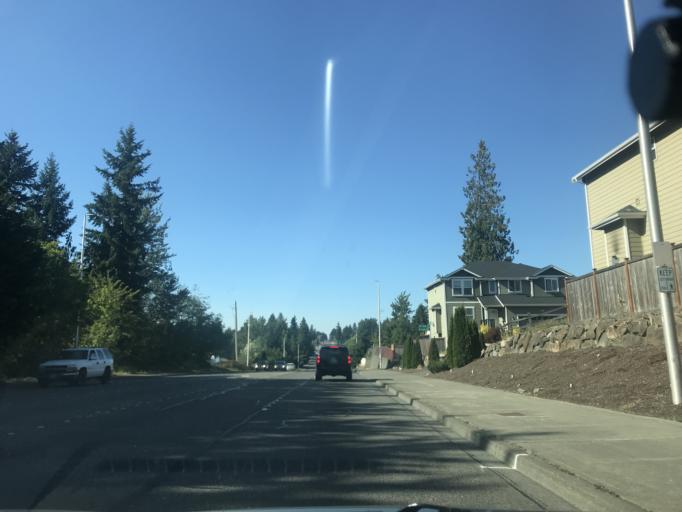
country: US
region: Washington
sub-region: King County
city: Lea Hill
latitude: 47.3624
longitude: -122.1867
